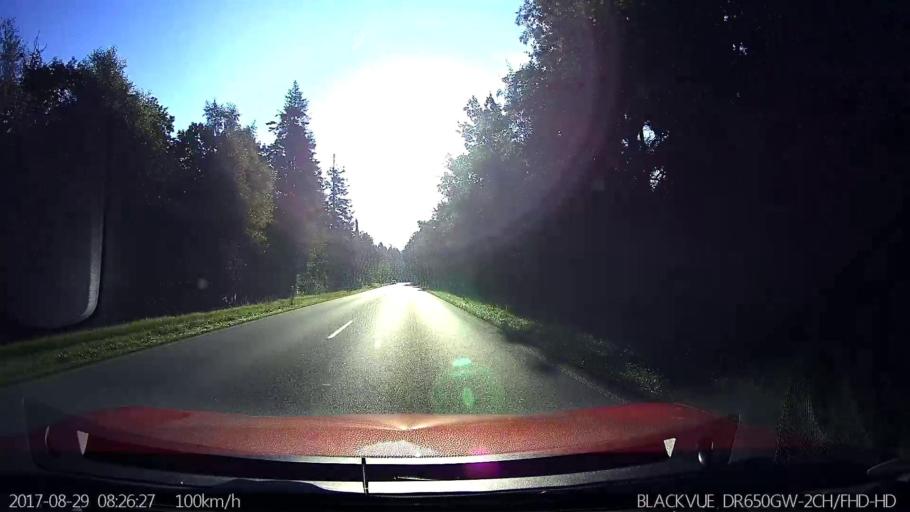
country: DE
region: Schleswig-Holstein
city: Schmalfeld
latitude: 53.9035
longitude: 9.9527
